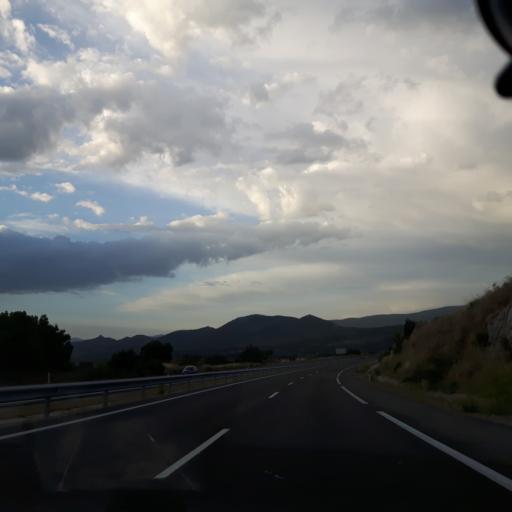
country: ES
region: Castille and Leon
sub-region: Provincia de Salamanca
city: Nava de Bejar
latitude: 40.4675
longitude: -5.6796
